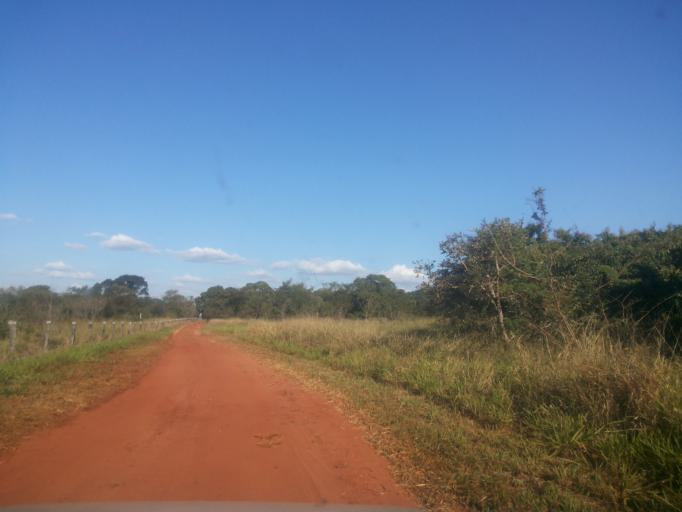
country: BR
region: Minas Gerais
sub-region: Santa Vitoria
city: Santa Vitoria
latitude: -19.0161
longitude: -50.4478
